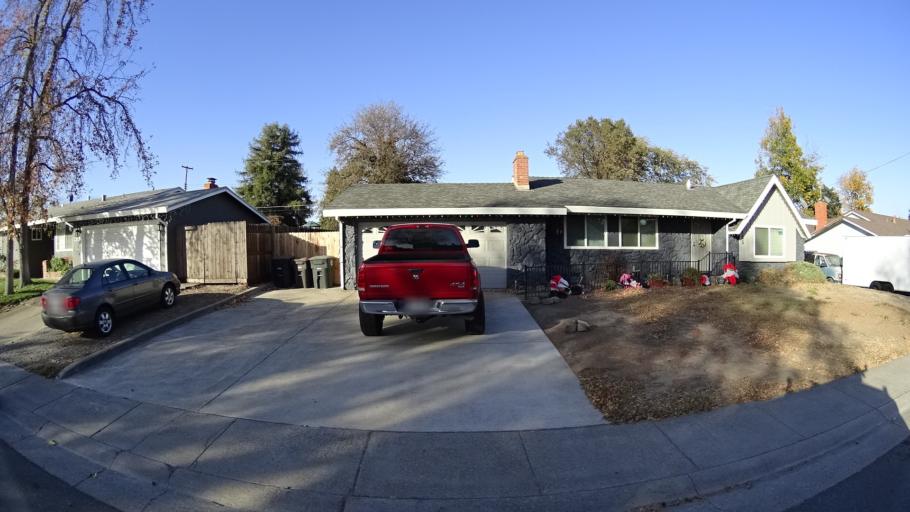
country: US
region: California
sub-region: Sacramento County
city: Citrus Heights
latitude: 38.6946
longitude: -121.2983
